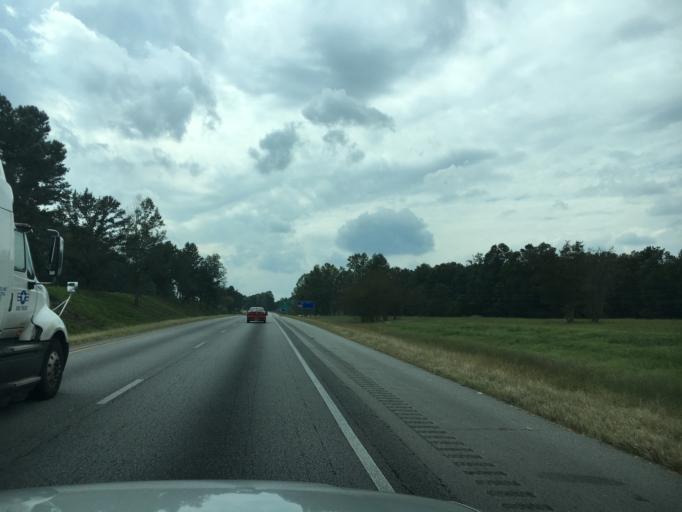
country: US
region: Georgia
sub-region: Franklin County
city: Gumlog
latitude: 34.4781
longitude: -83.0422
